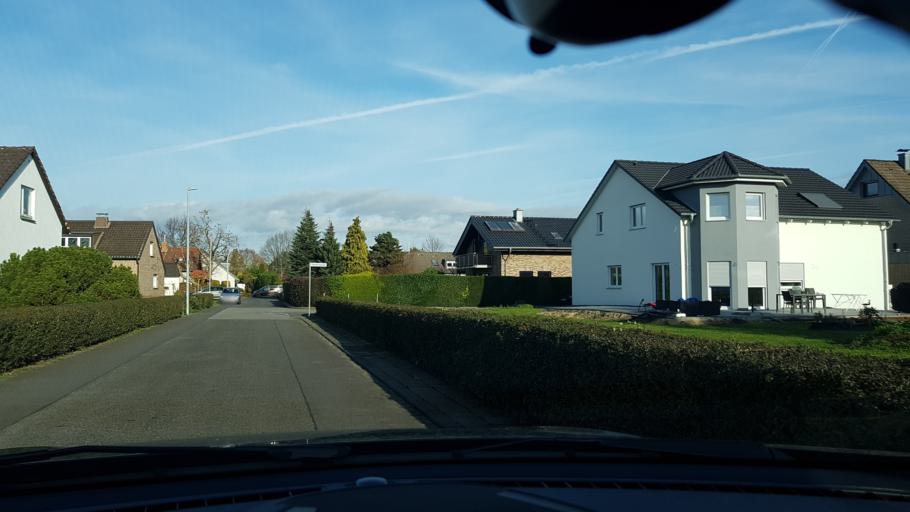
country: DE
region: North Rhine-Westphalia
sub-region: Regierungsbezirk Dusseldorf
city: Grevenbroich
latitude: 51.1147
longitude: 6.5590
